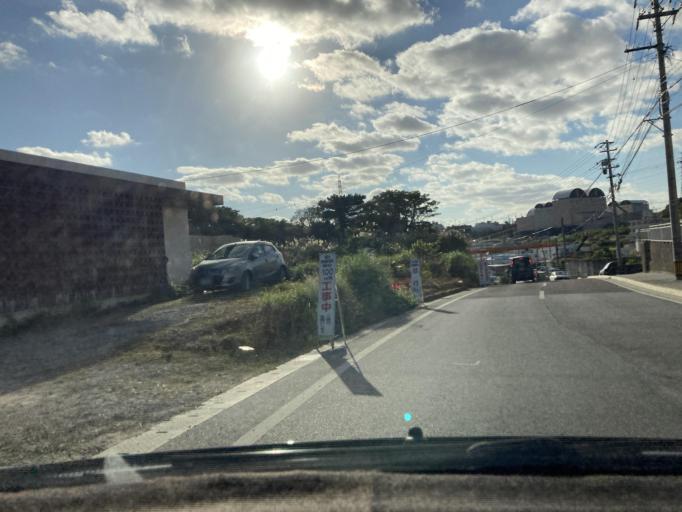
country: JP
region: Okinawa
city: Gushikawa
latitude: 26.3582
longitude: 127.8550
